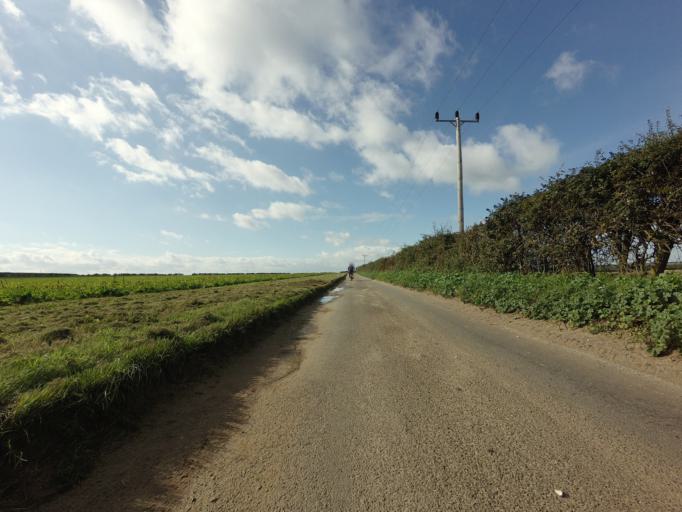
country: GB
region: England
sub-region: Norfolk
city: Hunstanton
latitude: 52.9361
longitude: 0.6207
